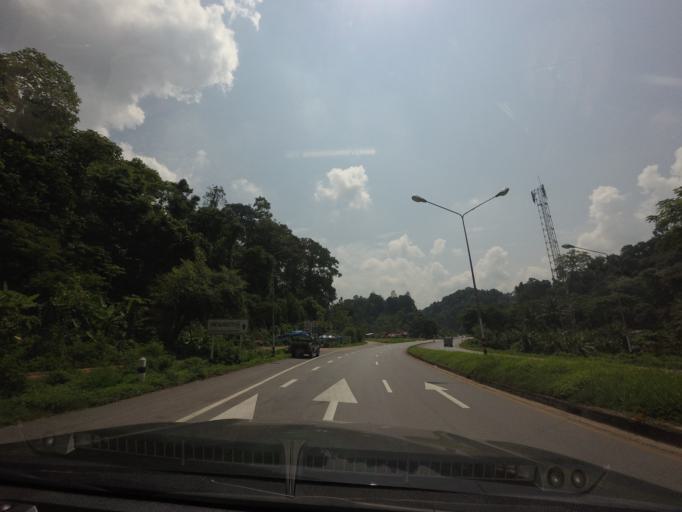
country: TH
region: Uttaradit
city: Lap Lae
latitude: 17.8097
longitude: 100.1084
